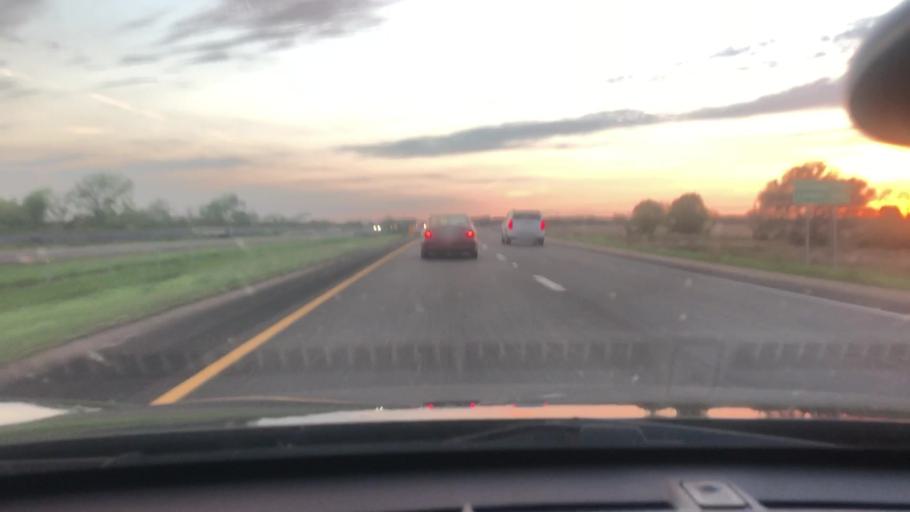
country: US
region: Texas
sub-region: Victoria County
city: Inez
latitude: 28.9237
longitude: -96.7538
